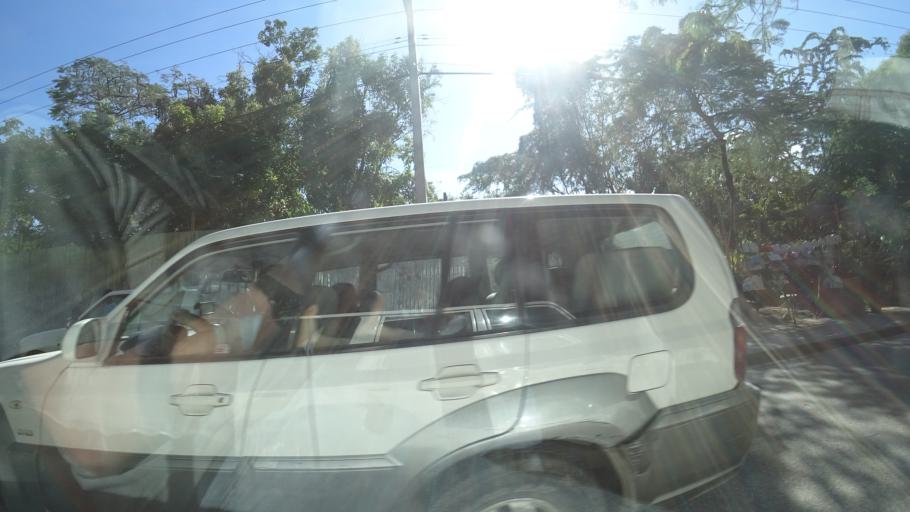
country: HT
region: Ouest
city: Delmas 73
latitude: 18.5321
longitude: -72.3024
